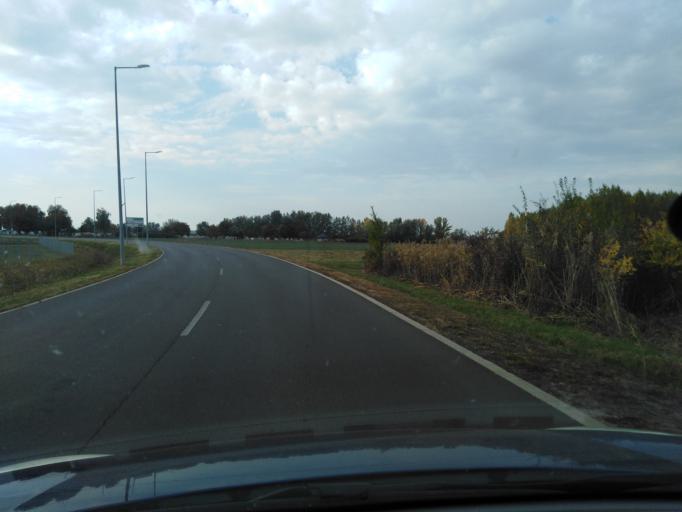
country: HU
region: Heves
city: Hatvan
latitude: 47.6783
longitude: 19.6628
